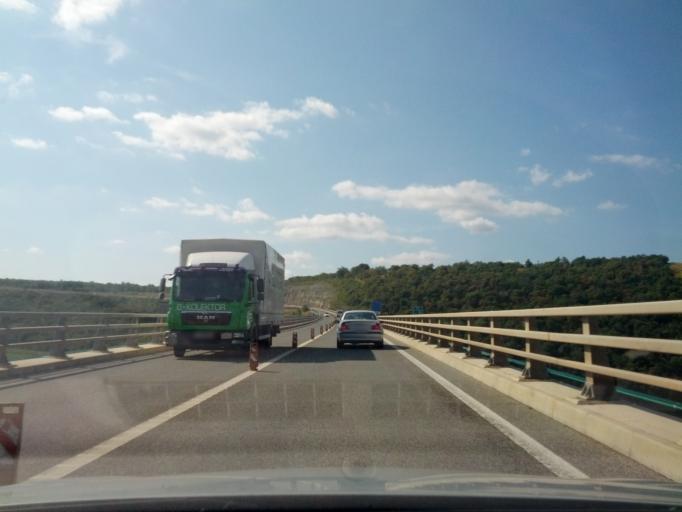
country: HR
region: Istarska
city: Novigrad
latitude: 45.3307
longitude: 13.6262
